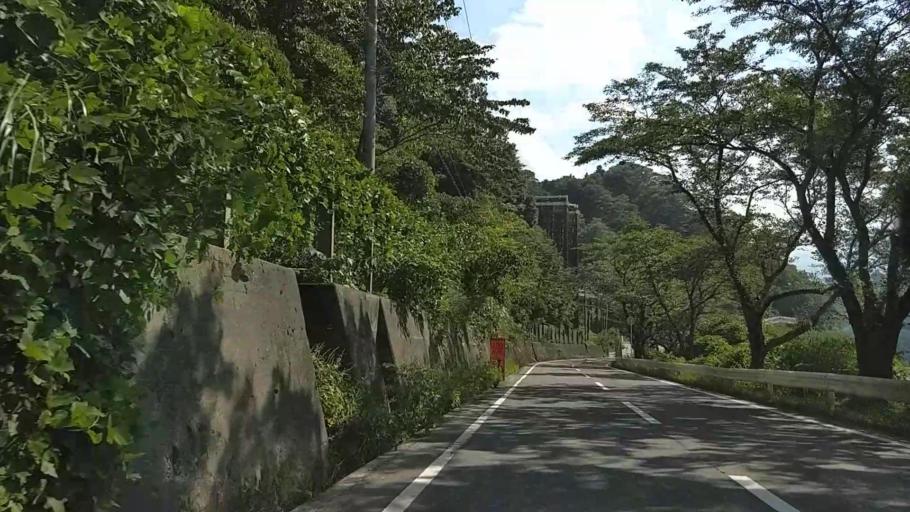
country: JP
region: Shizuoka
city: Fujinomiya
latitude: 35.4004
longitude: 138.4515
